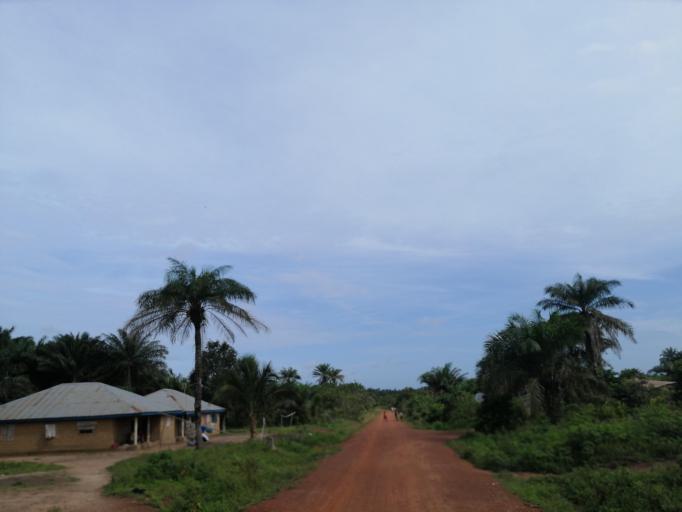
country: SL
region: Northern Province
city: Port Loko
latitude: 8.7671
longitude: -12.9046
